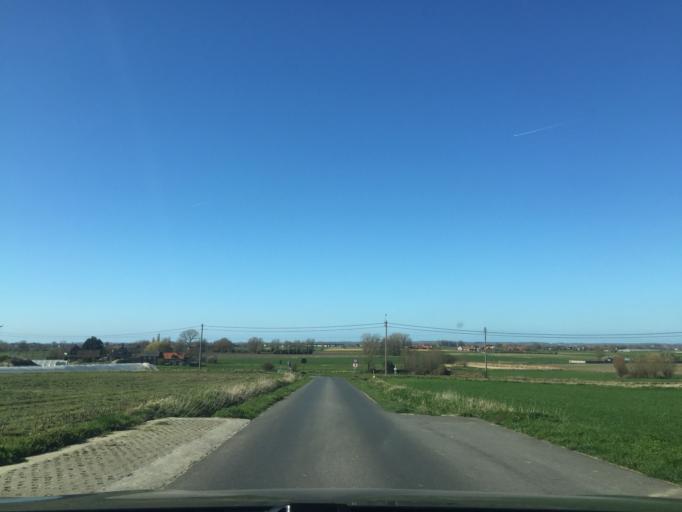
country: BE
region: Flanders
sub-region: Provincie West-Vlaanderen
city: Hooglede
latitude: 50.9842
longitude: 3.0774
